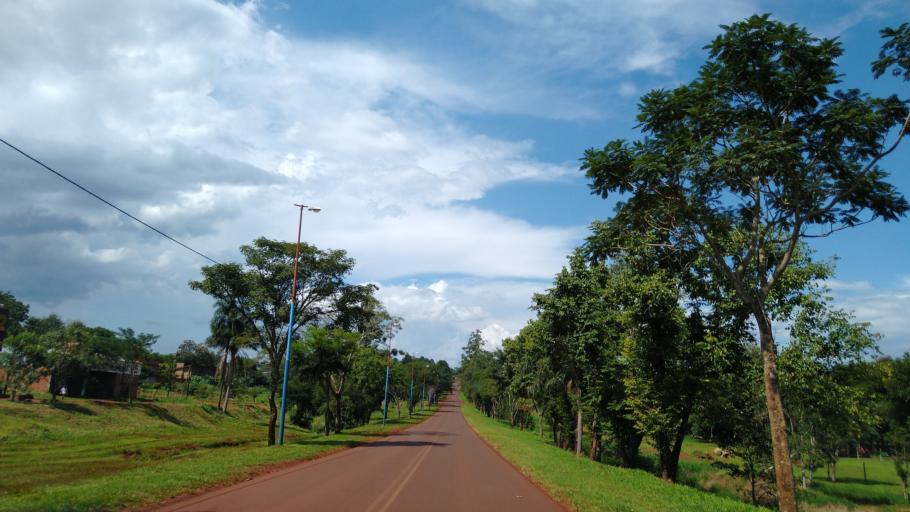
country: AR
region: Misiones
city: Puerto Libertad
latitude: -25.9704
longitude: -54.5669
